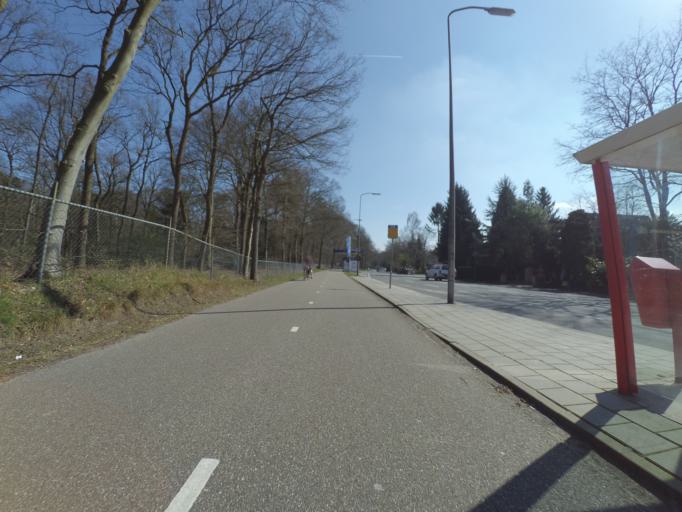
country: NL
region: Utrecht
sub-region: Gemeente Utrechtse Heuvelrug
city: Driebergen-Rijsenburg
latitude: 52.0408
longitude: 5.3086
